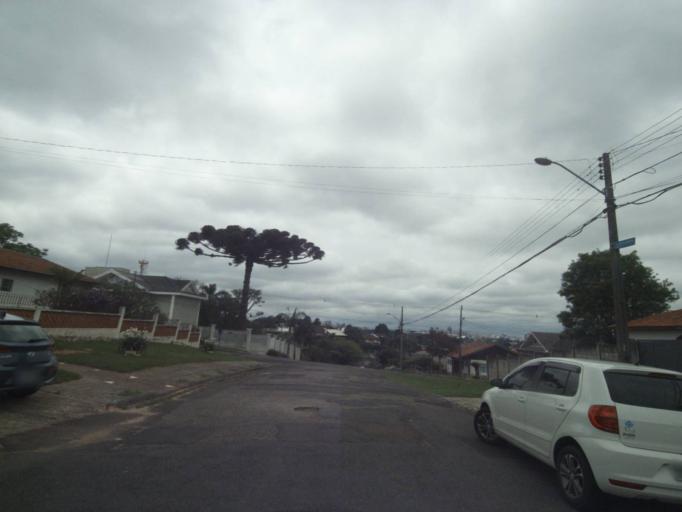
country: BR
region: Parana
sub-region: Curitiba
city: Curitiba
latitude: -25.3888
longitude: -49.2738
